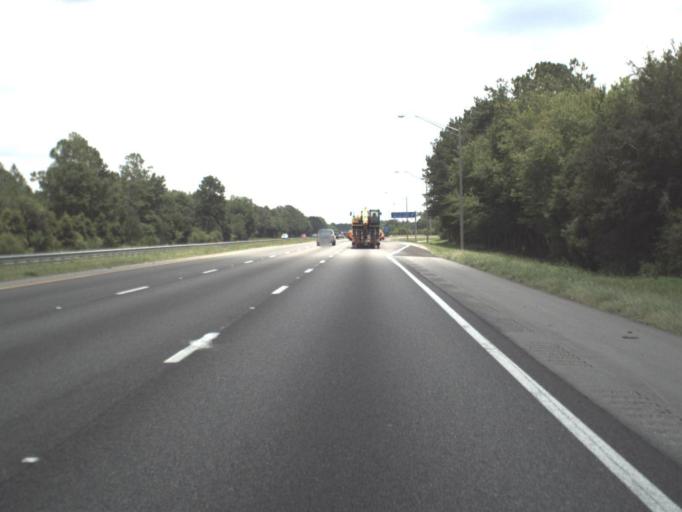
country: US
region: Georgia
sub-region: Echols County
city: Statenville
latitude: 30.6163
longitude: -83.1524
